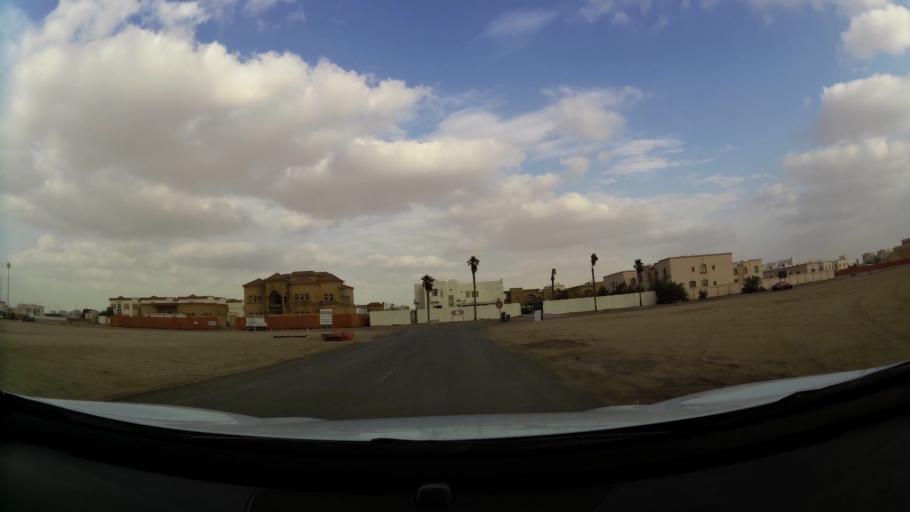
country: AE
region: Abu Dhabi
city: Abu Dhabi
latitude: 24.3673
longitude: 54.5444
